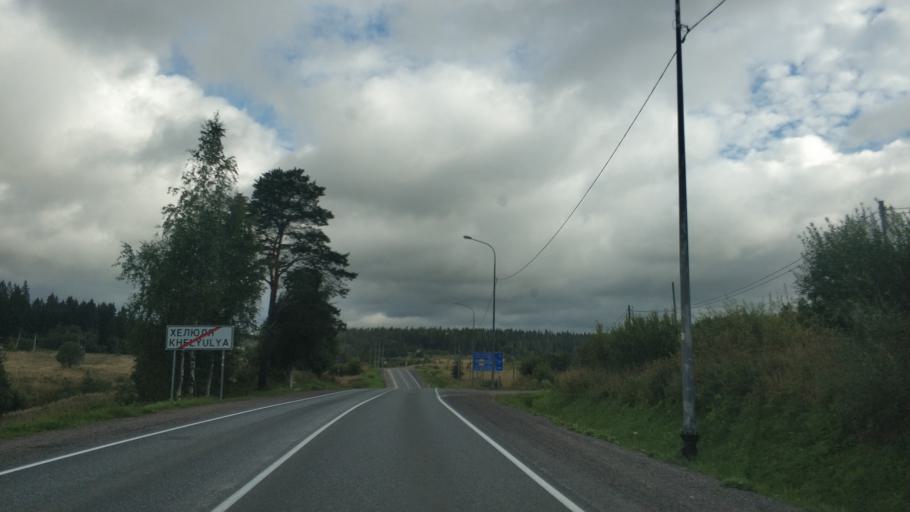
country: RU
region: Republic of Karelia
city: Khelyulya
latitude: 61.7566
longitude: 30.6568
